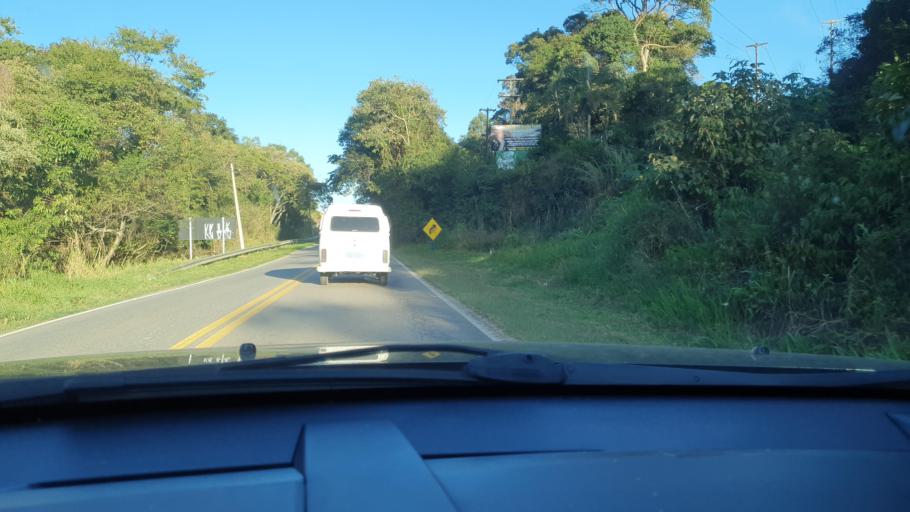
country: BR
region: Sao Paulo
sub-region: Piedade
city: Piedade
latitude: -23.7156
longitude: -47.3652
